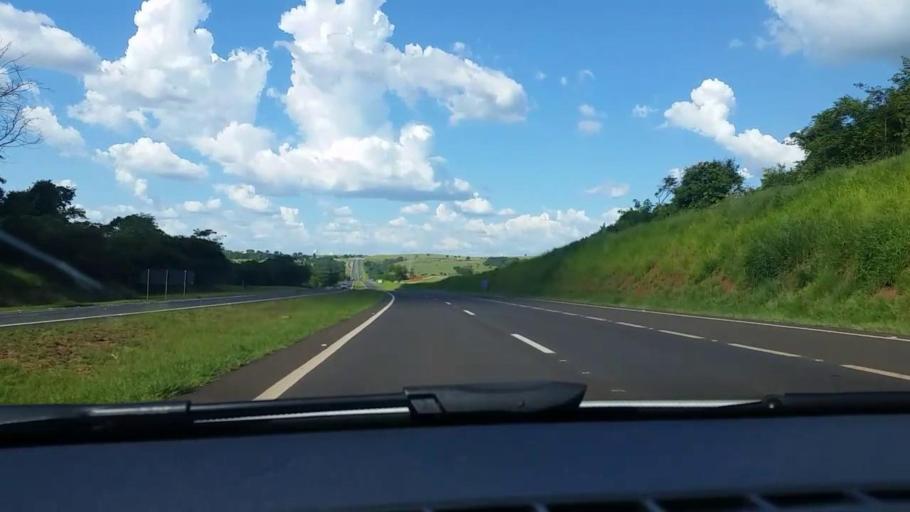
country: BR
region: Sao Paulo
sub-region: Bauru
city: Bauru
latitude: -22.4155
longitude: -49.1077
